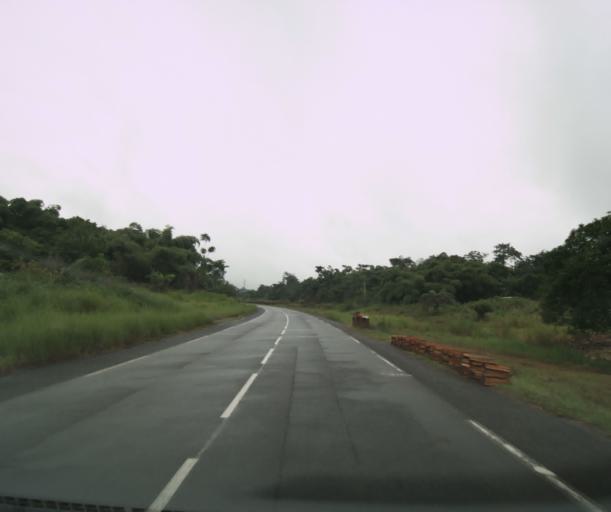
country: CM
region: Littoral
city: Dizangue
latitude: 3.3749
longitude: 10.1027
